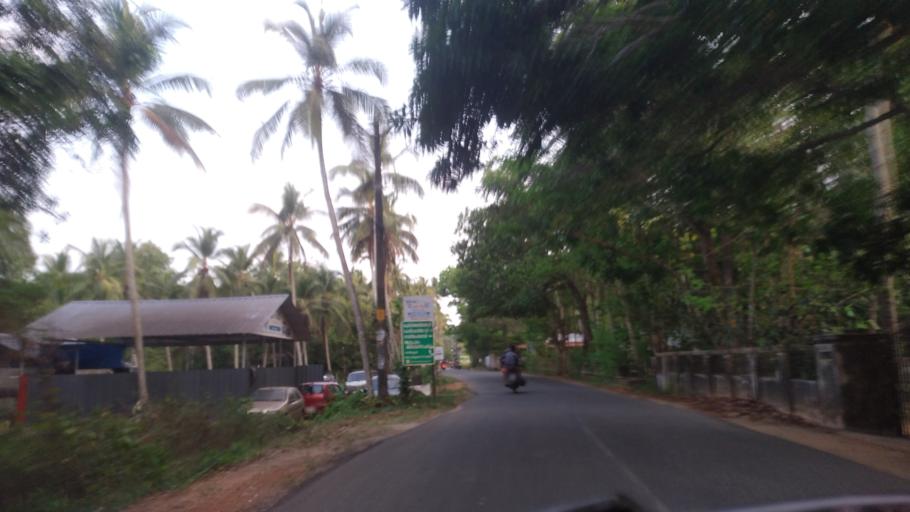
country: IN
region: Kerala
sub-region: Thrissur District
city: Kodungallur
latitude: 10.2538
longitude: 76.1471
